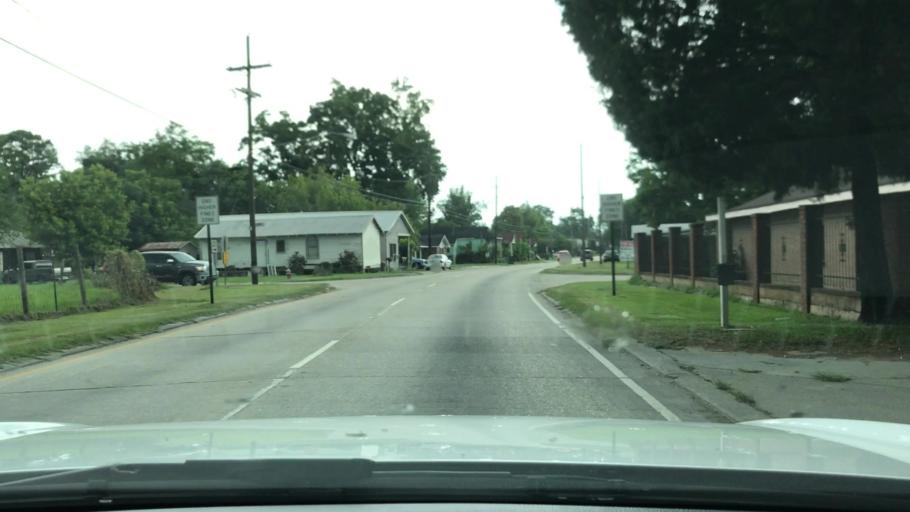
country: US
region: Louisiana
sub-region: Iberville Parish
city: Plaquemine
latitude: 30.2833
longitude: -91.2279
